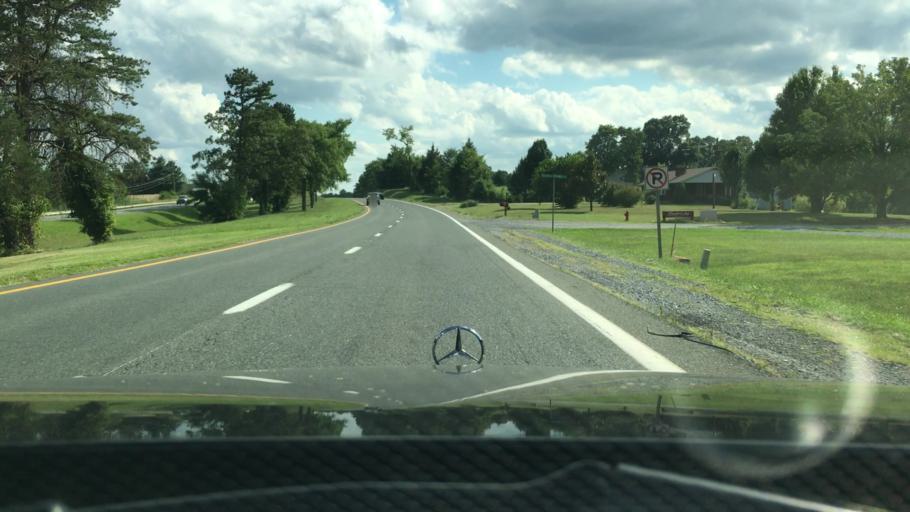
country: US
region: Virginia
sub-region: Campbell County
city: Altavista
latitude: 37.1735
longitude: -79.2078
